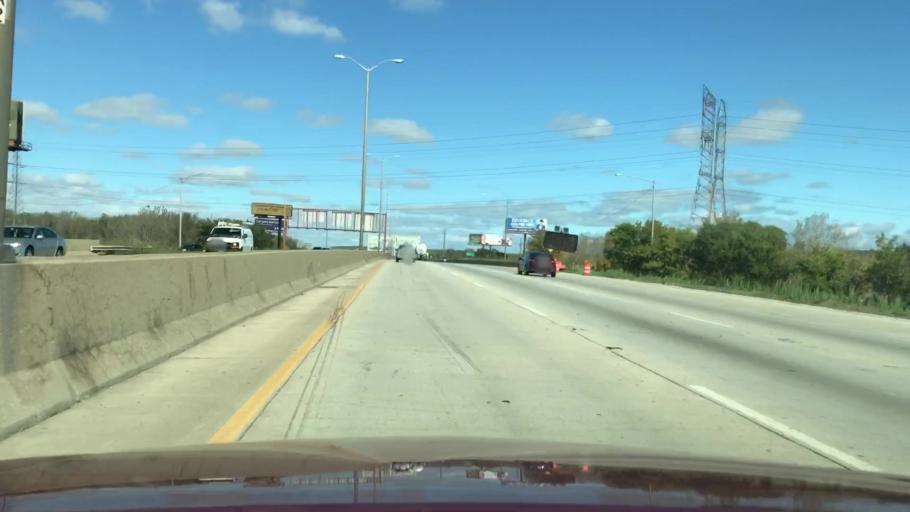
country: US
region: Illinois
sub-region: Cook County
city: Burnham
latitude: 41.6350
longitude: -87.5784
